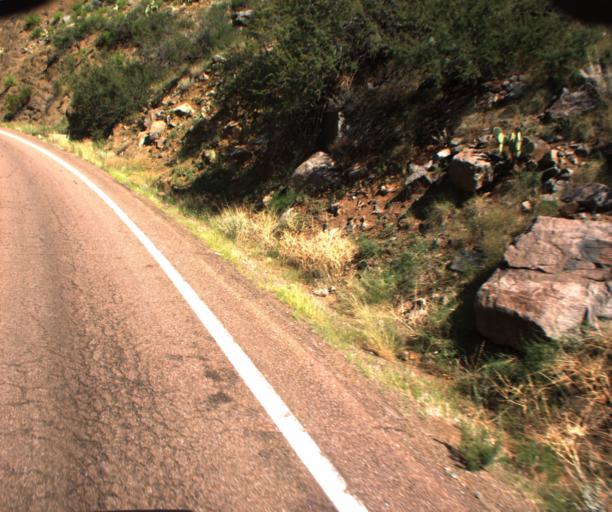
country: US
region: Arizona
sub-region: Navajo County
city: Cibecue
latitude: 33.7987
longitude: -110.4917
